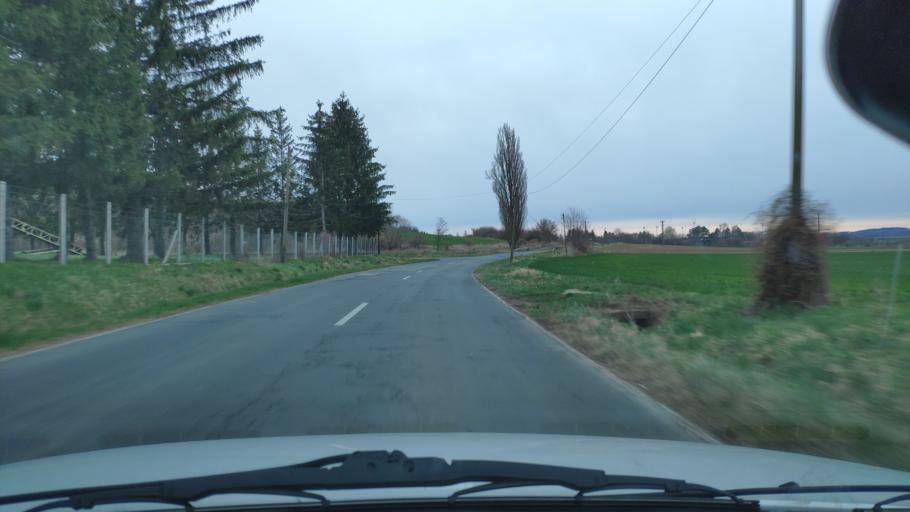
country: HU
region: Zala
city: Nagykanizsa
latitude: 46.5524
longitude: 16.9892
